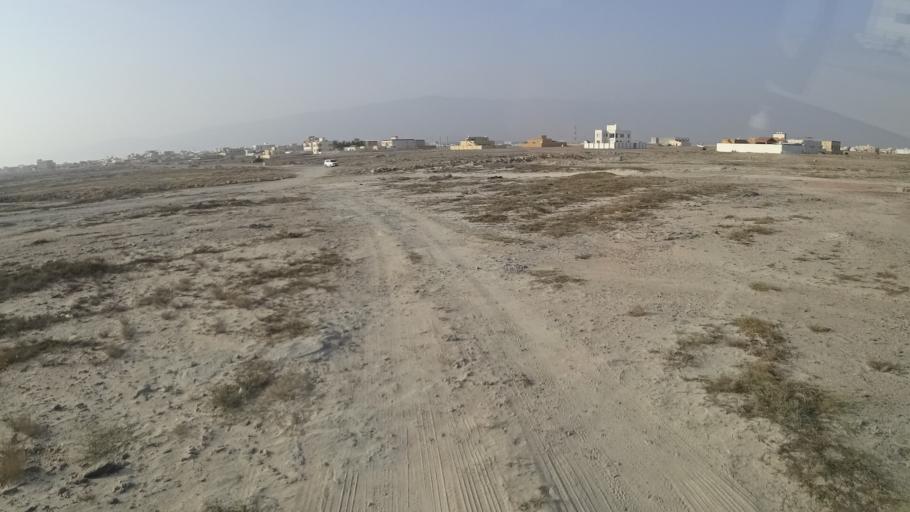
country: OM
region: Zufar
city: Salalah
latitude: 16.9737
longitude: 54.7007
